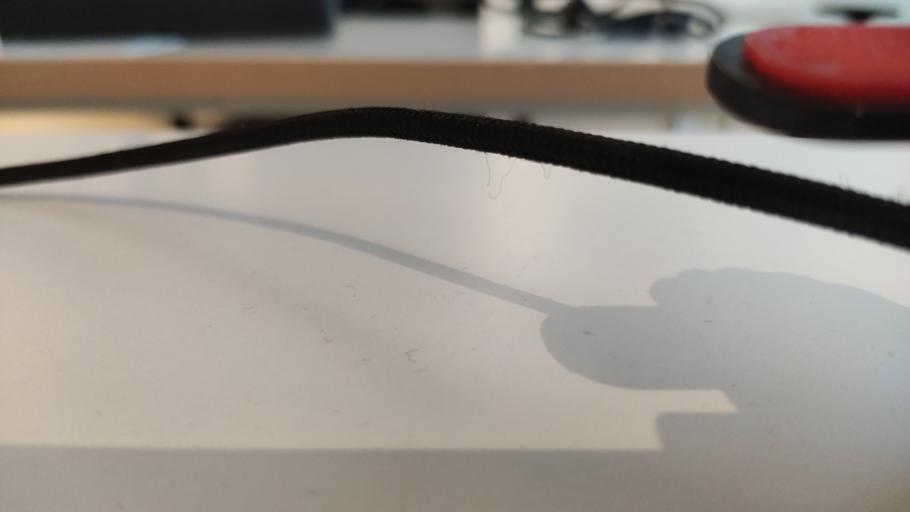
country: RU
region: Moskovskaya
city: Novopetrovskoye
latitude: 55.9393
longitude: 36.4355
